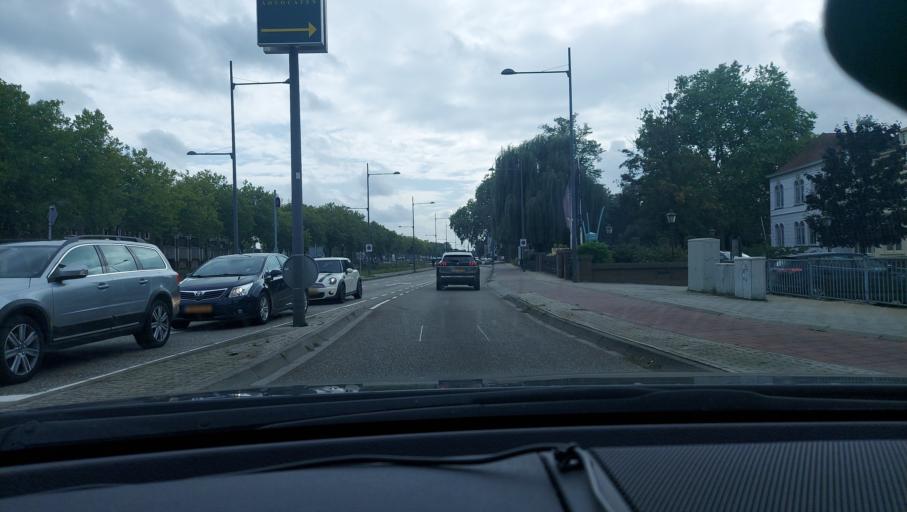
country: NL
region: North Brabant
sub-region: Gemeente Helmond
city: Helmond
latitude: 51.4852
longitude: 5.6513
